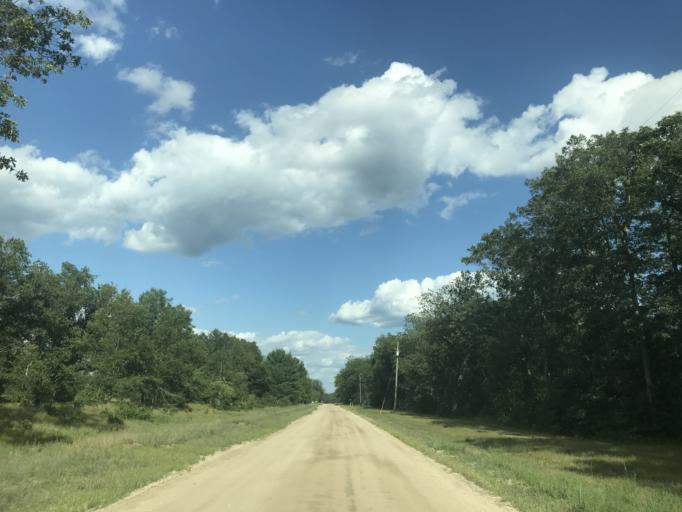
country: US
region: Michigan
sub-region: Newaygo County
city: Newaygo
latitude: 43.4492
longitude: -85.7551
